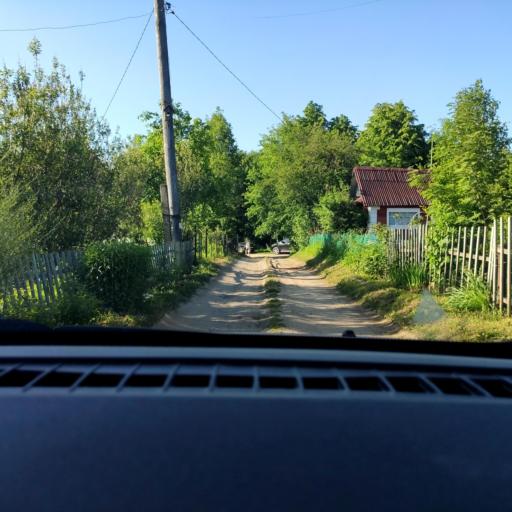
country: RU
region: Perm
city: Overyata
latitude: 58.1193
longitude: 55.8824
